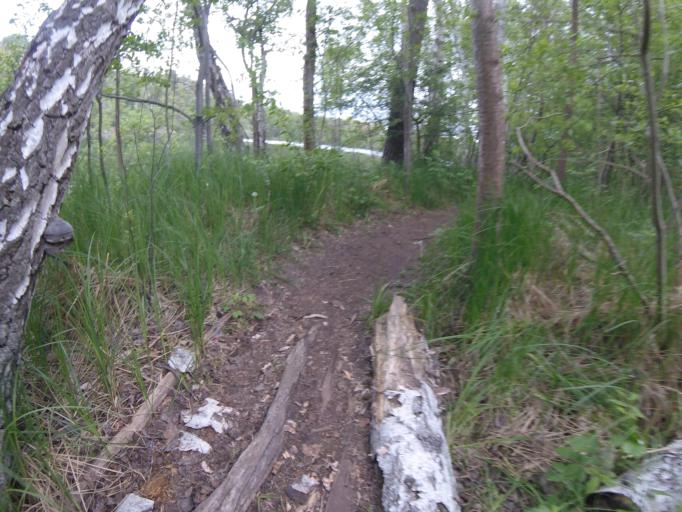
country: DE
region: Brandenburg
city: Bestensee
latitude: 52.2505
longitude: 13.6668
